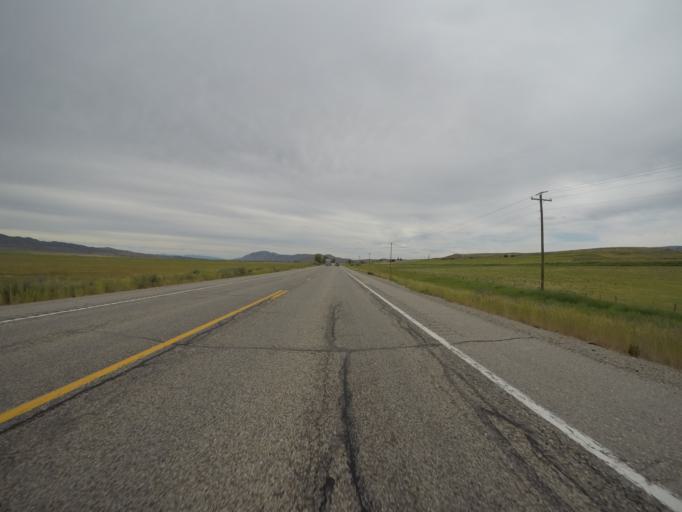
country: US
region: Utah
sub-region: Rich County
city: Randolph
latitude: 42.0277
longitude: -110.9325
